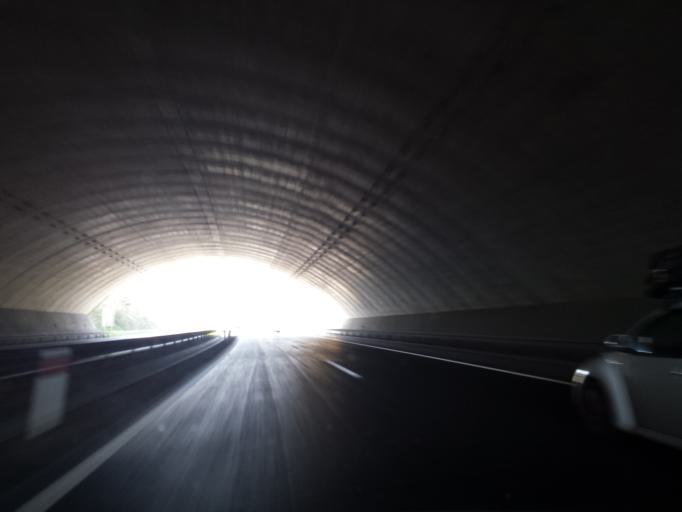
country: HR
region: Karlovacka
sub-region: Grad Ogulin
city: Ogulin
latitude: 45.3736
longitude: 15.2695
